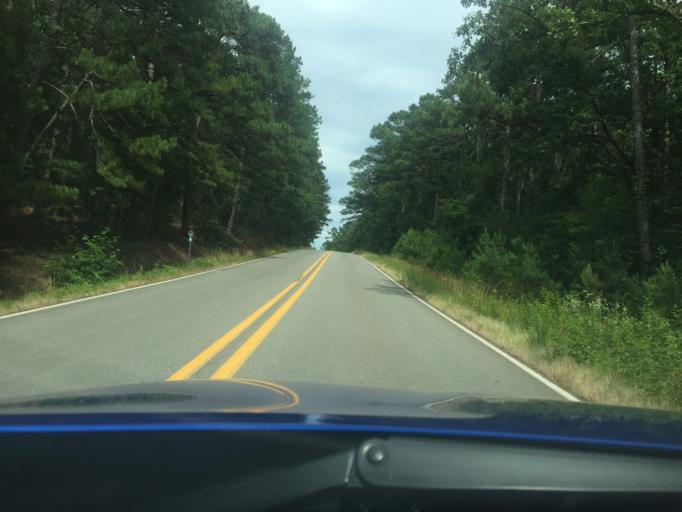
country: US
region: Arkansas
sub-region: Pulaski County
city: Maumelle
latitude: 34.8350
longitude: -92.4627
